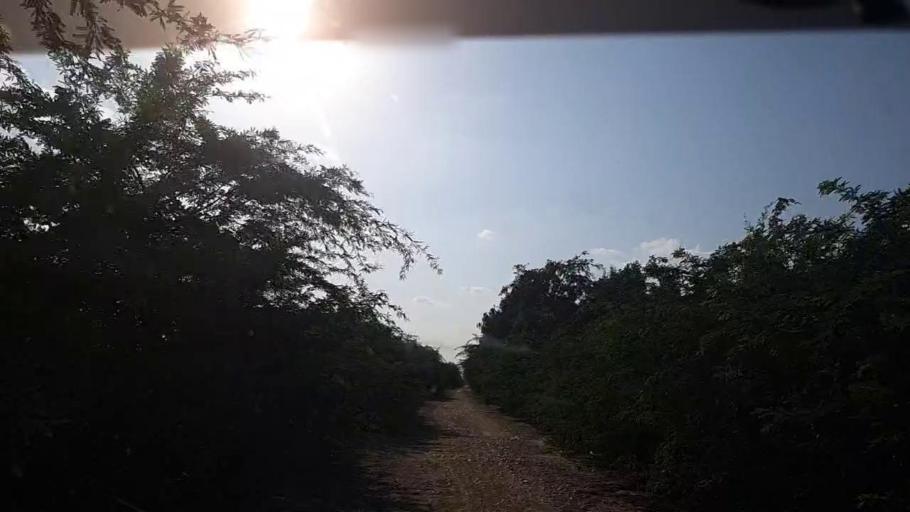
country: PK
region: Sindh
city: Kadhan
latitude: 24.4417
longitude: 68.9977
